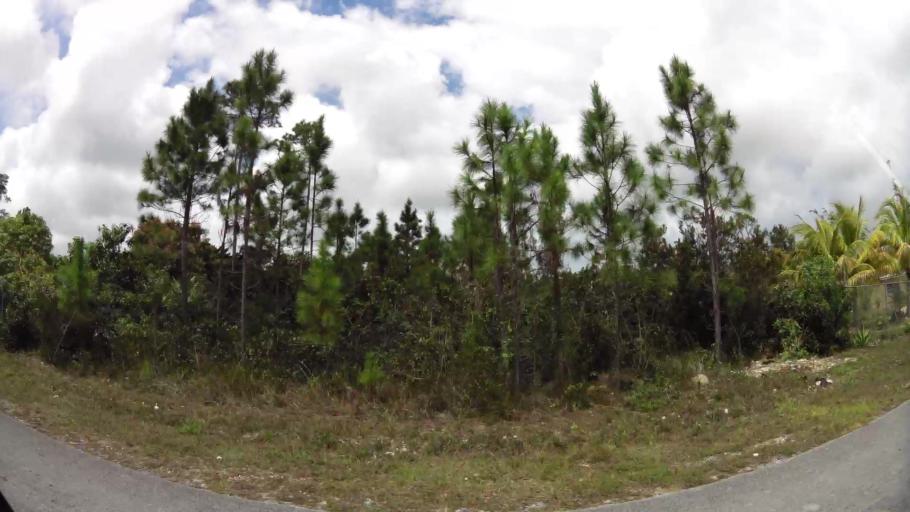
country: BS
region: Freeport
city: Lucaya
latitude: 26.5445
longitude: -78.6449
